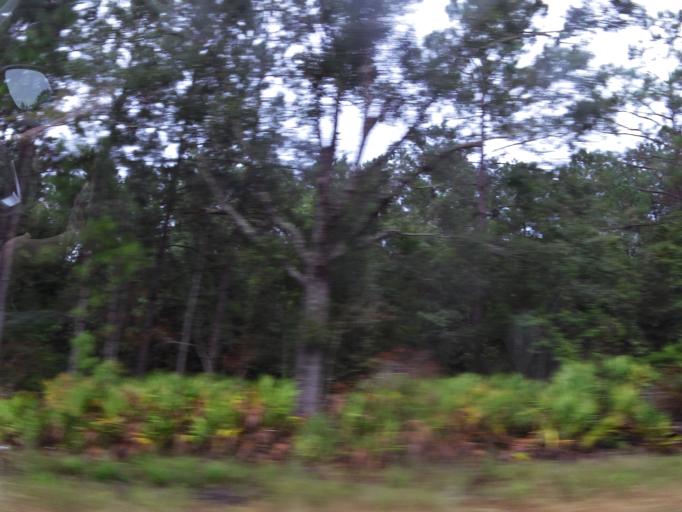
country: US
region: Georgia
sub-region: Wayne County
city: Jesup
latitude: 31.5161
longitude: -81.7731
